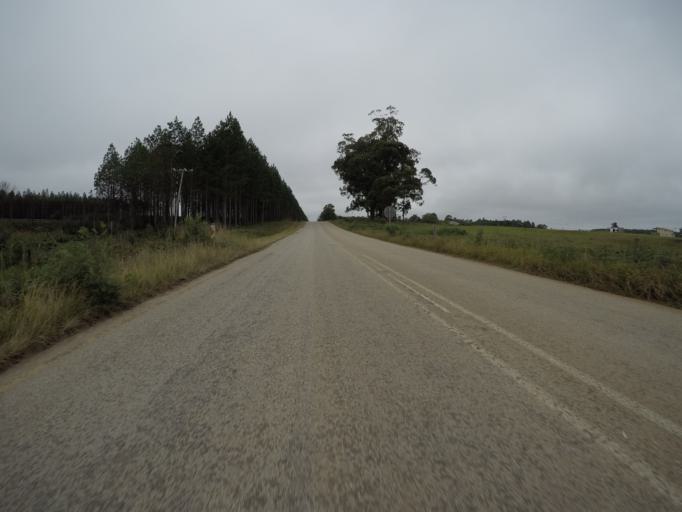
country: ZA
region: Eastern Cape
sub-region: Cacadu District Municipality
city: Kareedouw
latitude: -33.9902
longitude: 24.0828
